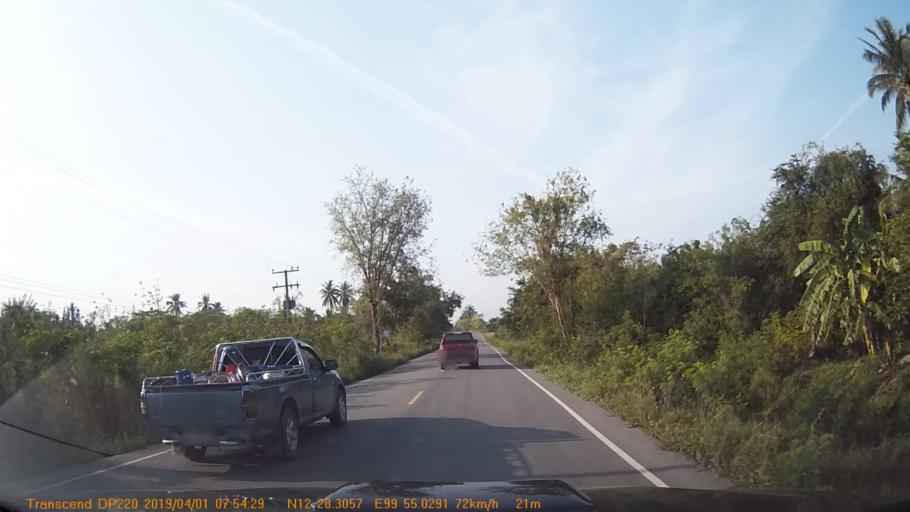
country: TH
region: Prachuap Khiri Khan
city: Pran Buri
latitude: 12.4714
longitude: 99.9172
